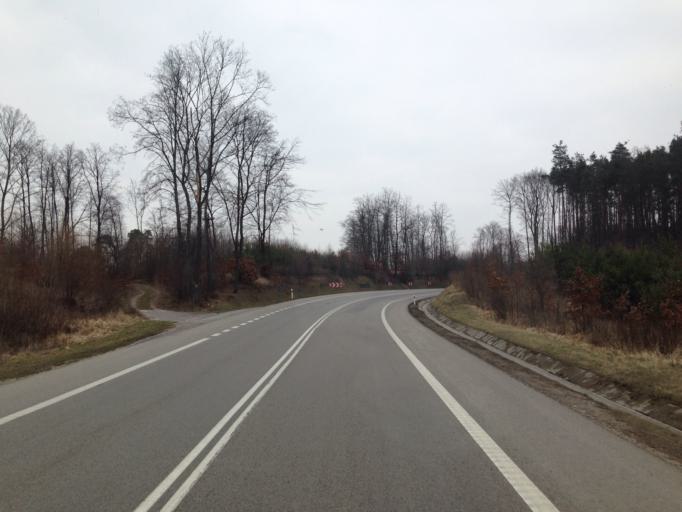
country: PL
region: Pomeranian Voivodeship
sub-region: Powiat starogardzki
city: Smetowo Graniczne
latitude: 53.7521
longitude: 18.7585
